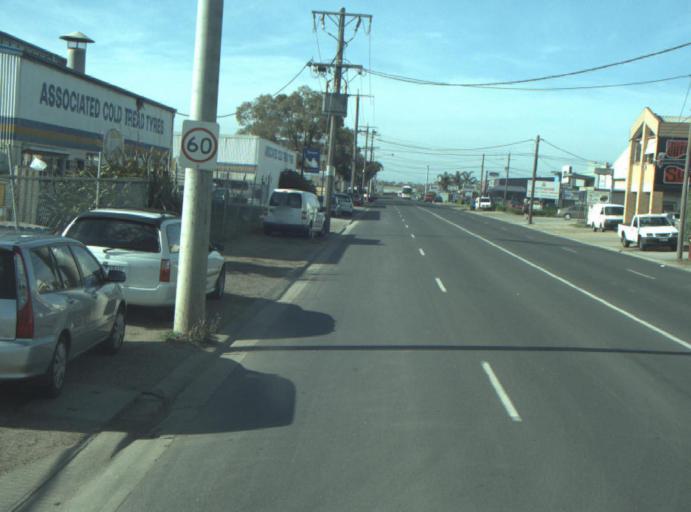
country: AU
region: Victoria
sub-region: Greater Geelong
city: Bell Park
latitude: -38.1154
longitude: 144.3491
